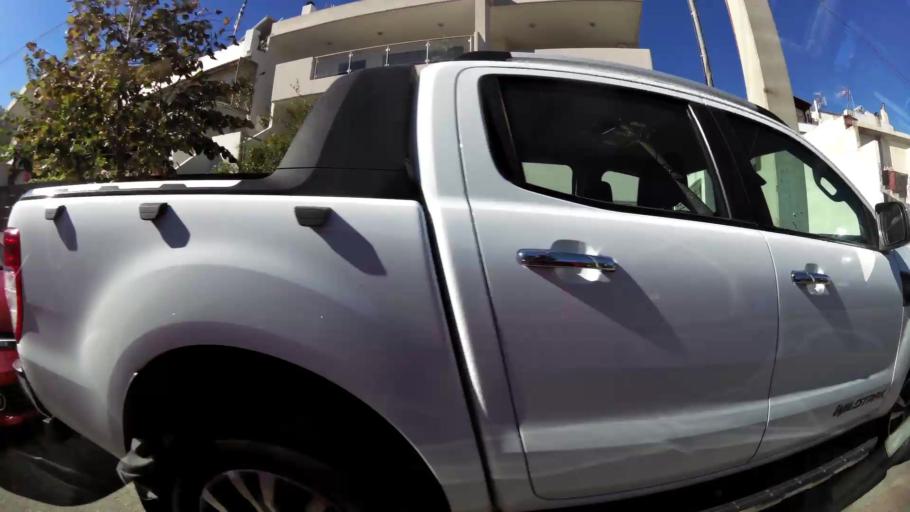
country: GR
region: Attica
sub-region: Nomarchia Anatolikis Attikis
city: Leondarion
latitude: 37.9997
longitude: 23.8584
